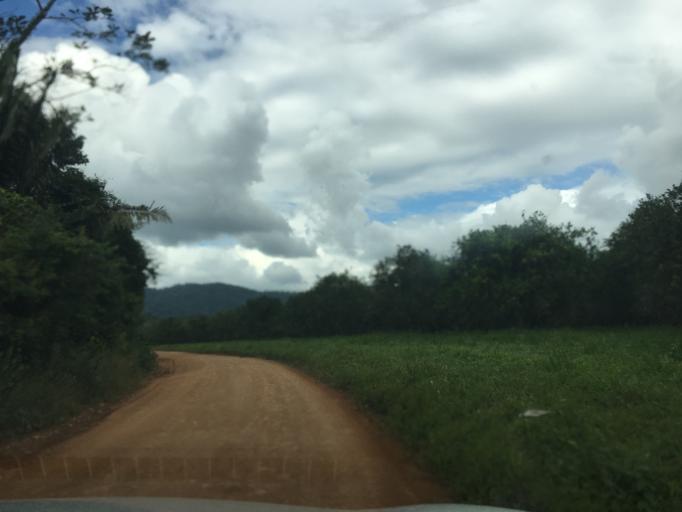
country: BZ
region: Stann Creek
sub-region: Dangriga
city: Dangriga
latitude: 16.9340
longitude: -88.3530
